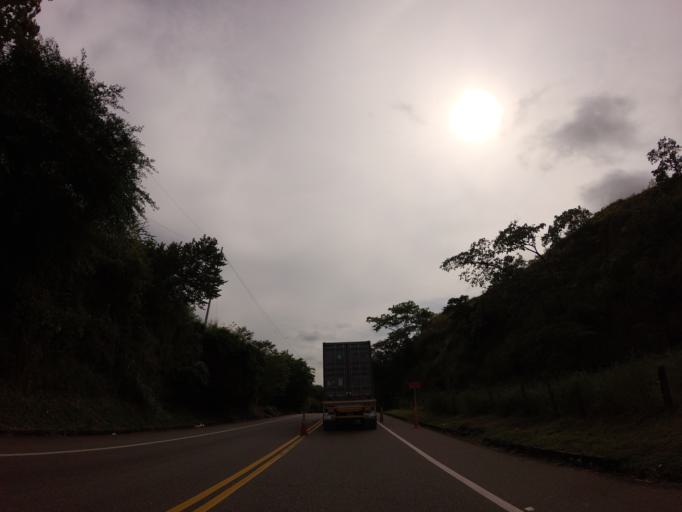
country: CO
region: Caldas
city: La Dorada
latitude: 5.4169
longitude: -74.6872
